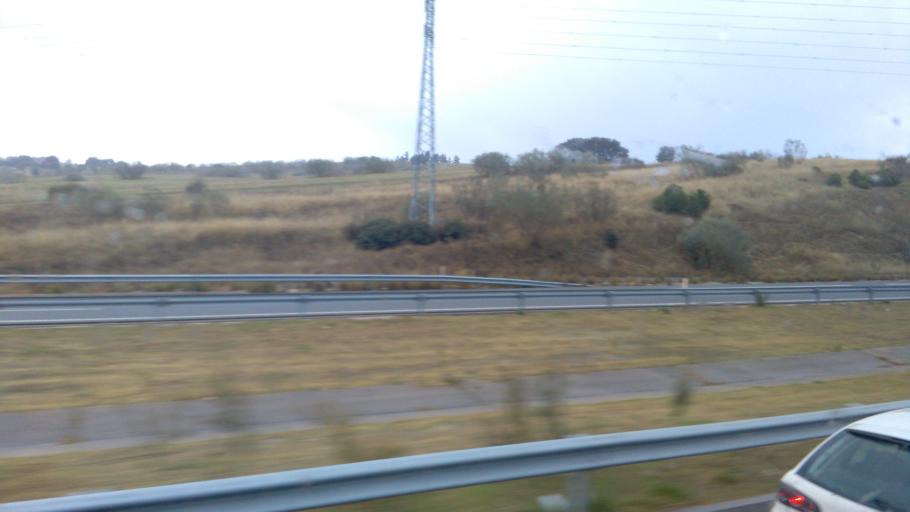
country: ES
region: Madrid
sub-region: Provincia de Madrid
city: Arroyomolinos
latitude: 40.2586
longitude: -3.9368
